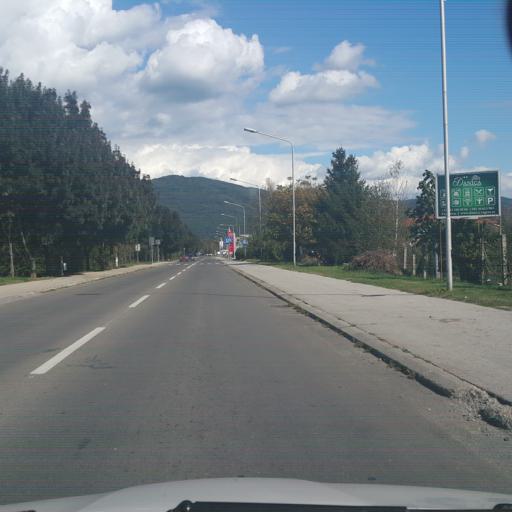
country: RS
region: Central Serbia
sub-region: Raski Okrug
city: Vrnjacka Banja
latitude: 43.6365
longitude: 20.9140
